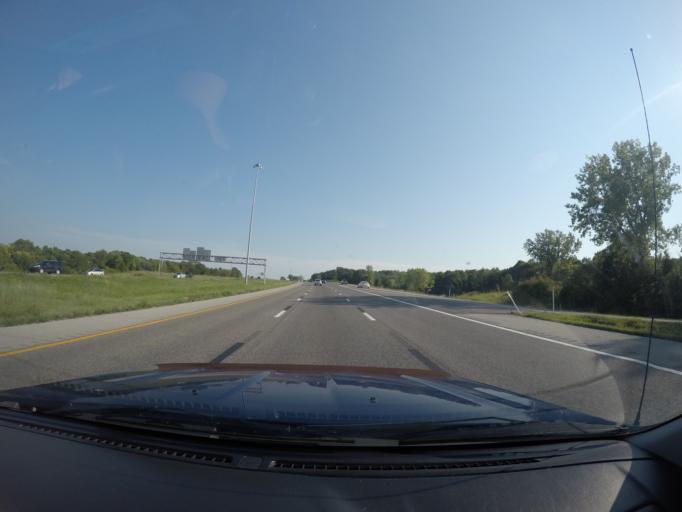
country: US
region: Kansas
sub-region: Wyandotte County
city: Edwardsville
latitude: 39.1011
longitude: -94.8111
